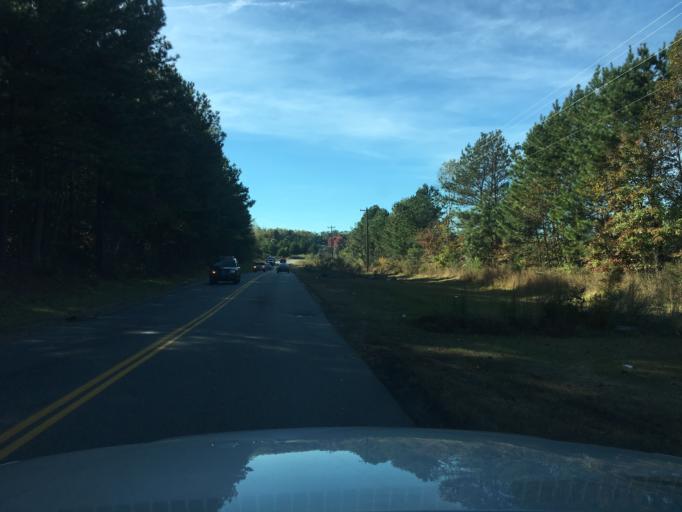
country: US
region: North Carolina
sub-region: Catawba County
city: Hickory
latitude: 35.7047
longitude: -81.2884
